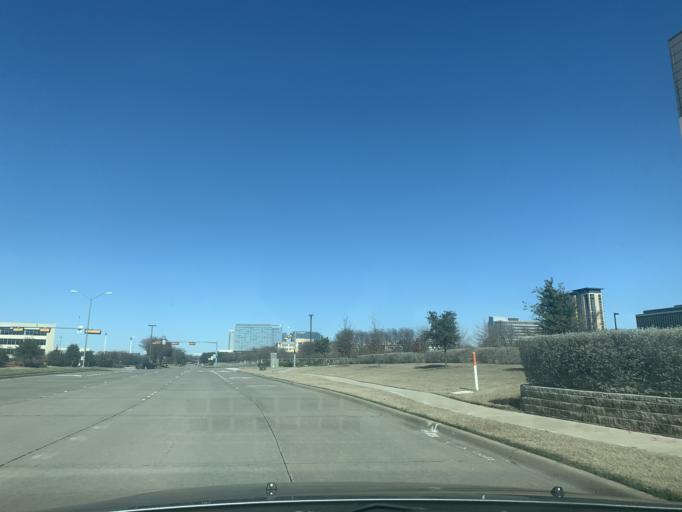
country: US
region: Texas
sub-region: Denton County
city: The Colony
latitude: 33.0711
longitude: -96.8283
